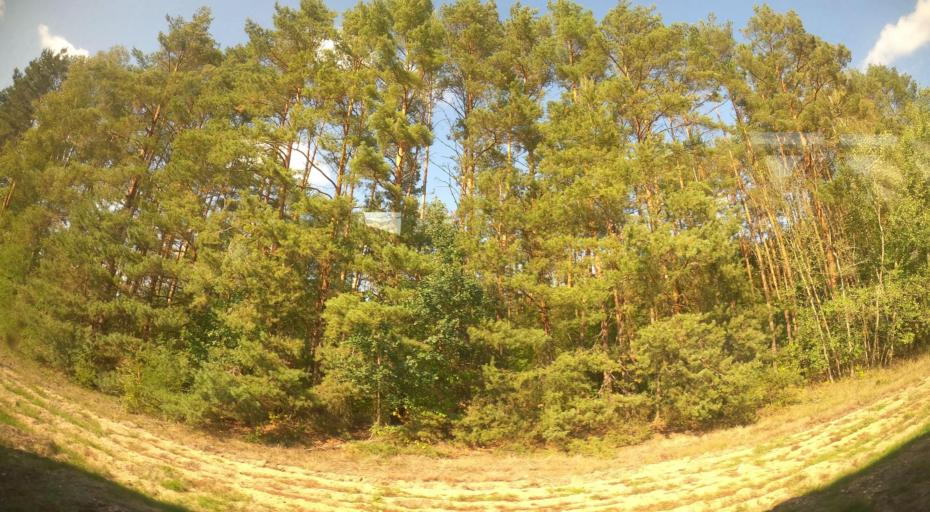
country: PL
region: Lubusz
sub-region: Powiat zielonogorski
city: Swidnica
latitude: 51.9310
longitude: 15.4006
